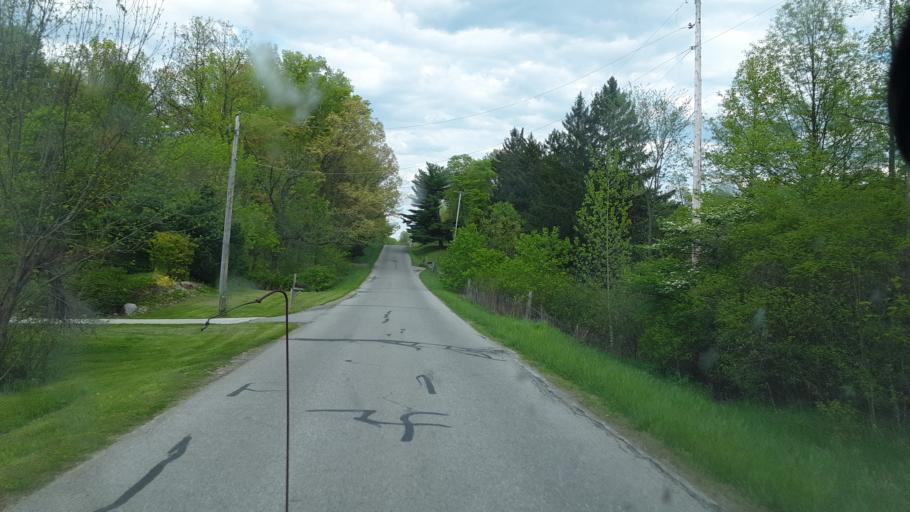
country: US
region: Ohio
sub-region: Portage County
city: Garrettsville
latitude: 41.3478
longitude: -81.0115
